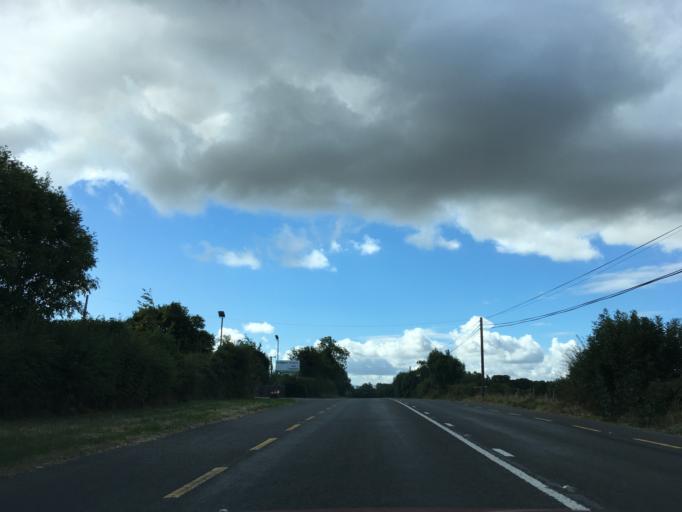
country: IE
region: Munster
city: Cahir
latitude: 52.4202
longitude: -7.8885
